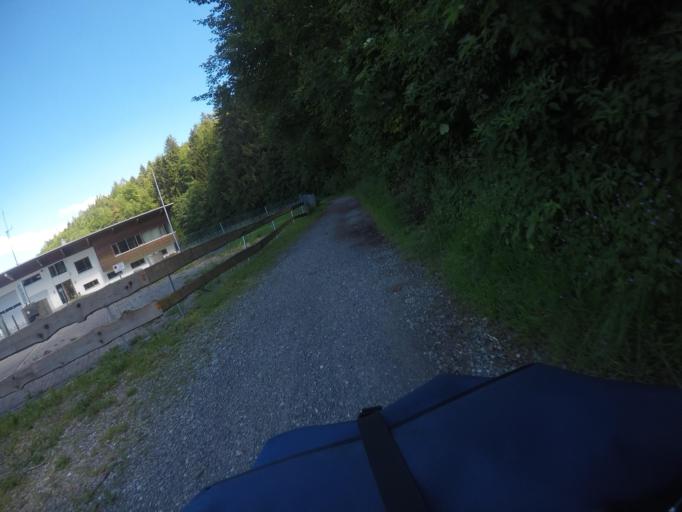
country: DE
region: Bavaria
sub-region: Swabia
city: Fuessen
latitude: 47.5670
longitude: 10.6817
